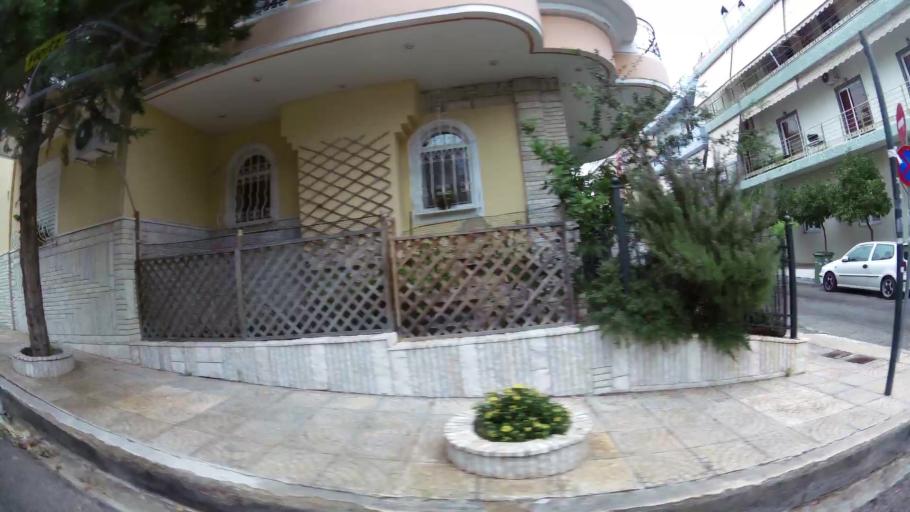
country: GR
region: Attica
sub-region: Nomos Piraios
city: Korydallos
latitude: 37.9858
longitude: 23.6474
